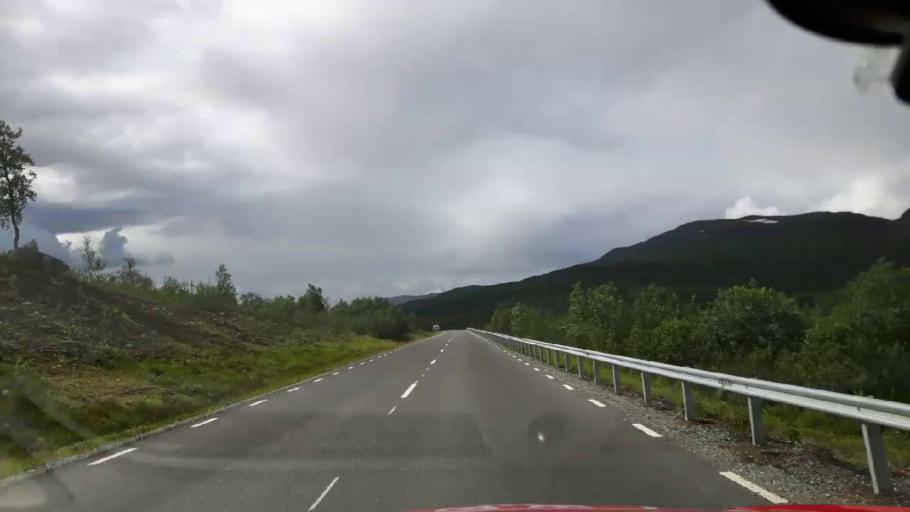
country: NO
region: Nordland
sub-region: Hattfjelldal
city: Hattfjelldal
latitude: 64.9899
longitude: 14.2202
